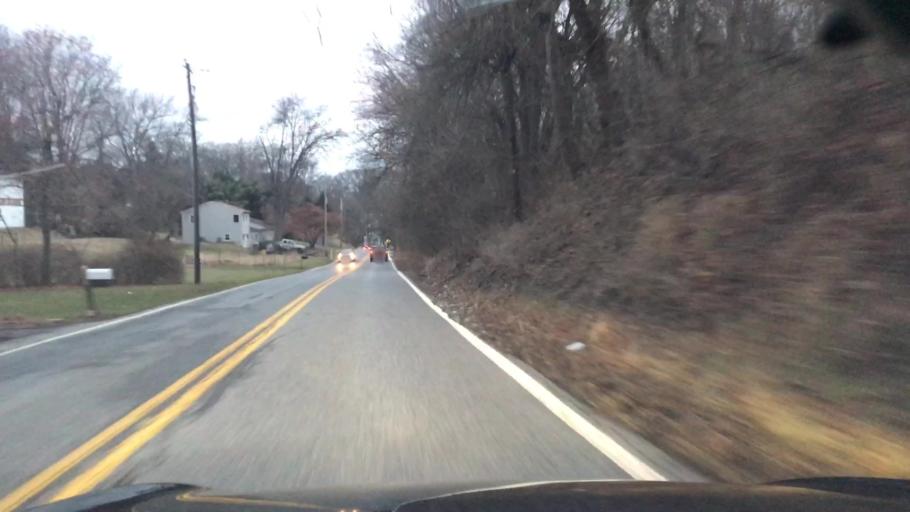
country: US
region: Pennsylvania
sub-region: Cumberland County
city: Lower Allen
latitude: 40.1662
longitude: -76.8996
